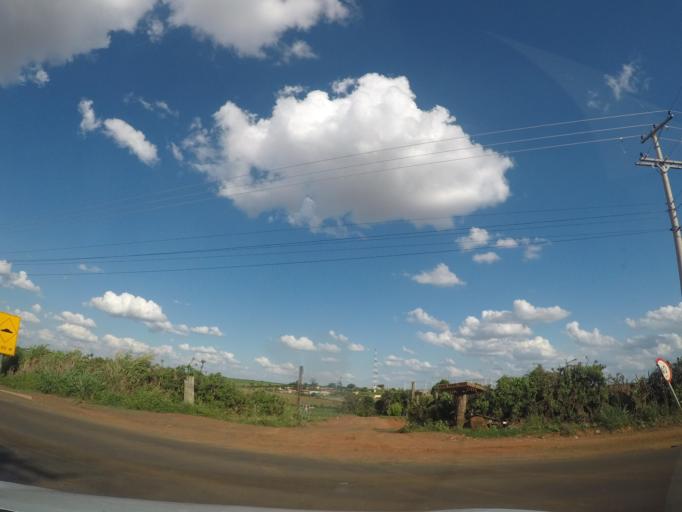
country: BR
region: Sao Paulo
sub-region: Sumare
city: Sumare
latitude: -22.8627
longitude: -47.2937
